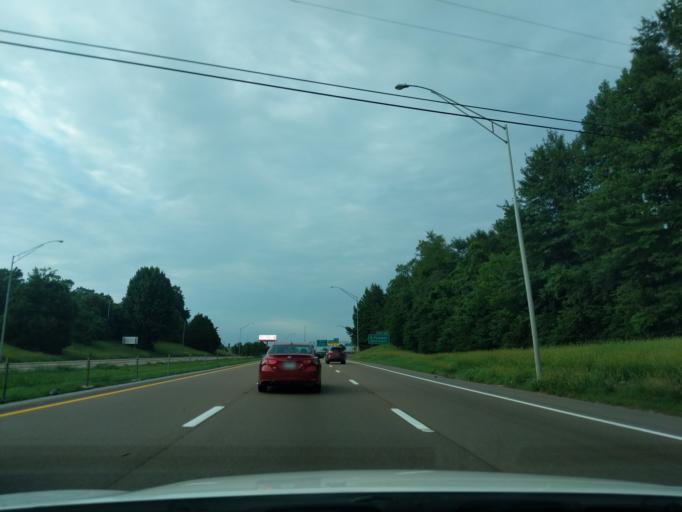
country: US
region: Tennessee
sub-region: Shelby County
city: New South Memphis
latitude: 35.1038
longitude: -90.0761
